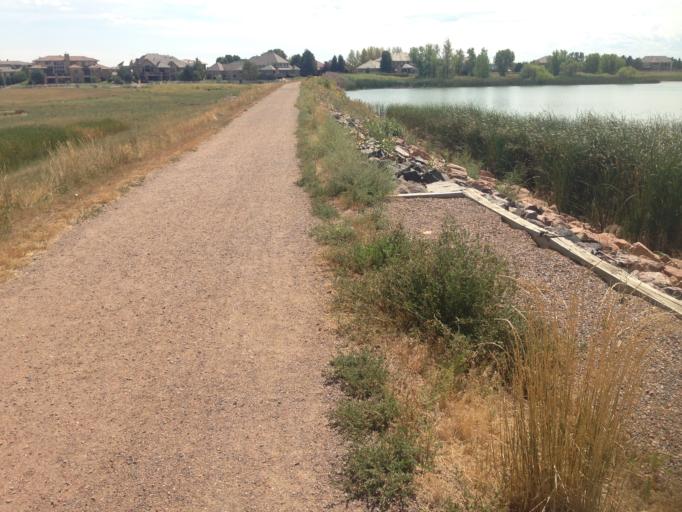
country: US
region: Colorado
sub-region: Adams County
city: Northglenn
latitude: 39.9561
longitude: -105.0086
